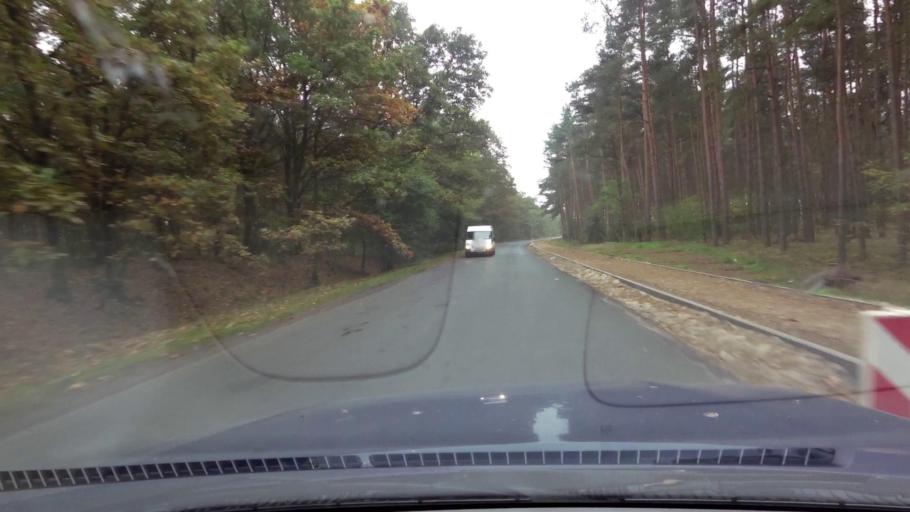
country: PL
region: West Pomeranian Voivodeship
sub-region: Powiat goleniowski
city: Goleniow
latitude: 53.5312
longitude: 14.7587
